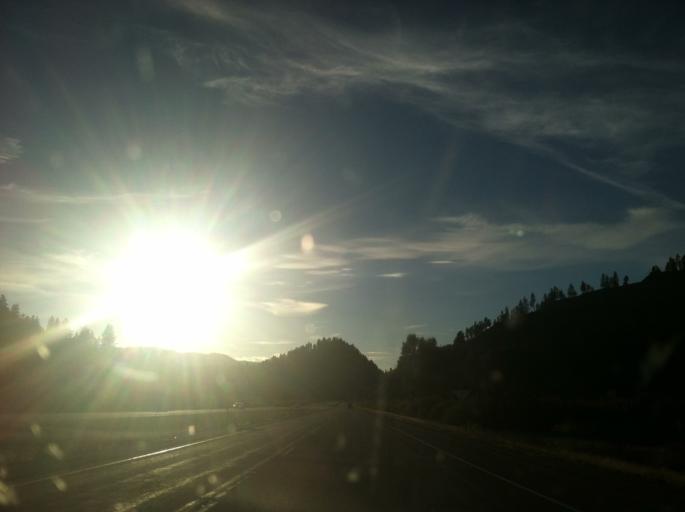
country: US
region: Montana
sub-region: Missoula County
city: Clinton
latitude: 46.6999
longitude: -113.4394
